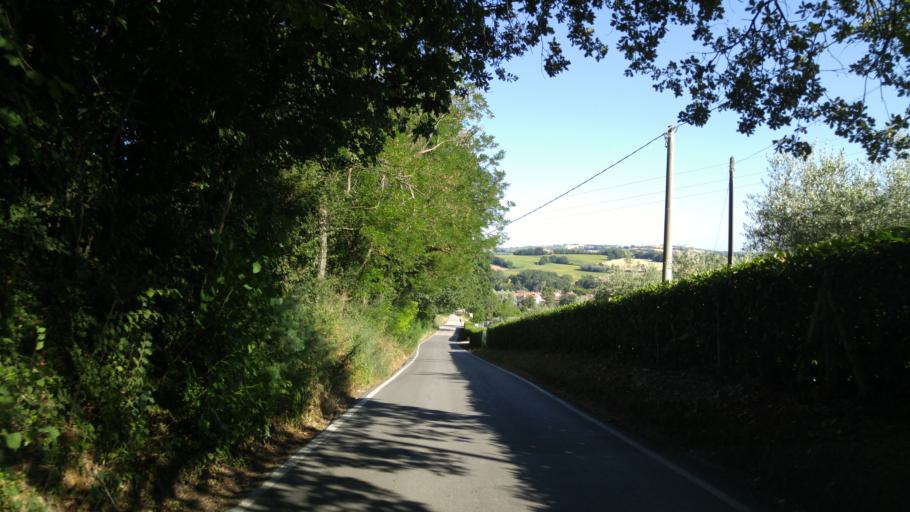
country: IT
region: The Marches
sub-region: Provincia di Pesaro e Urbino
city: Pesaro
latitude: 43.8467
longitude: 12.8923
